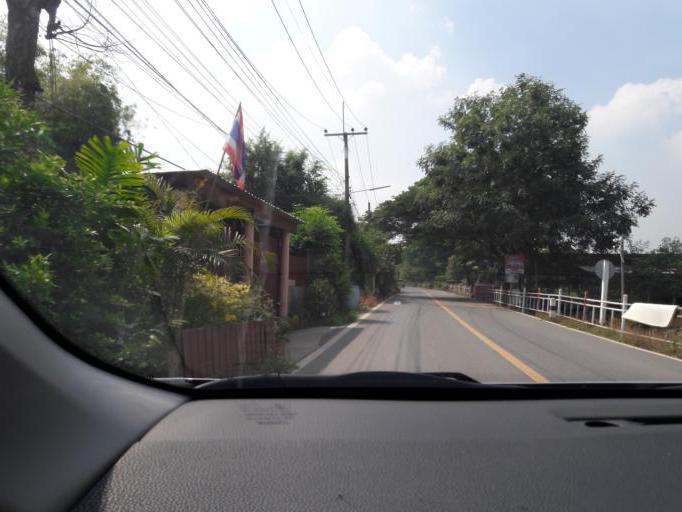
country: TH
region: Ang Thong
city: Ang Thong
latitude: 14.5607
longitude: 100.4275
